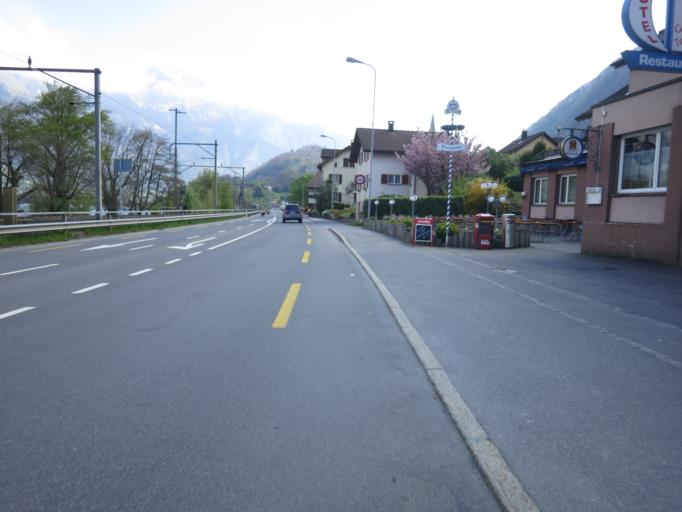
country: CH
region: Saint Gallen
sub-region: Wahlkreis Sarganserland
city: Walenstadt
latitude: 47.1126
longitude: 9.2786
